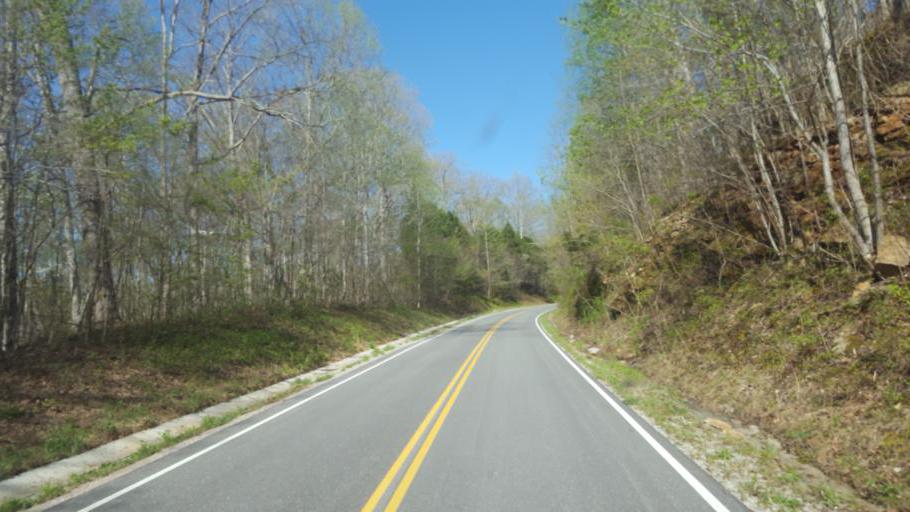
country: US
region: Kentucky
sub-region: Edmonson County
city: Brownsville
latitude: 37.1577
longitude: -86.1570
